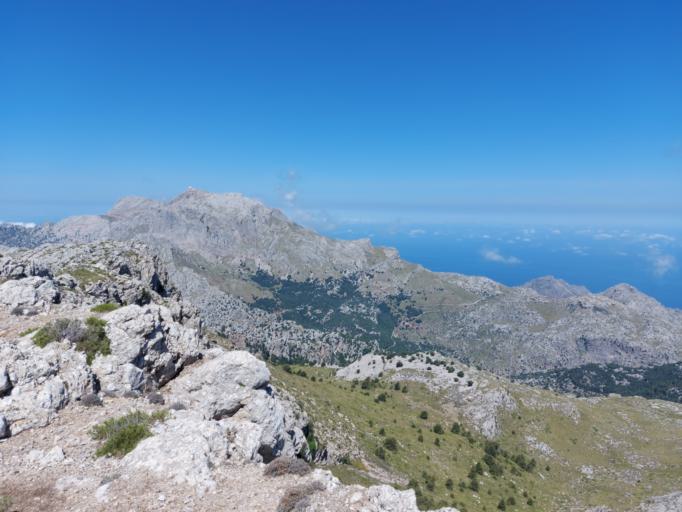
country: ES
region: Balearic Islands
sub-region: Illes Balears
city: Escorca
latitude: 39.8089
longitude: 2.8484
